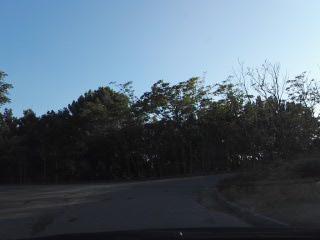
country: IT
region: Calabria
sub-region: Provincia di Vibo-Valentia
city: Nardodipace
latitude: 38.4288
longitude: 16.3409
